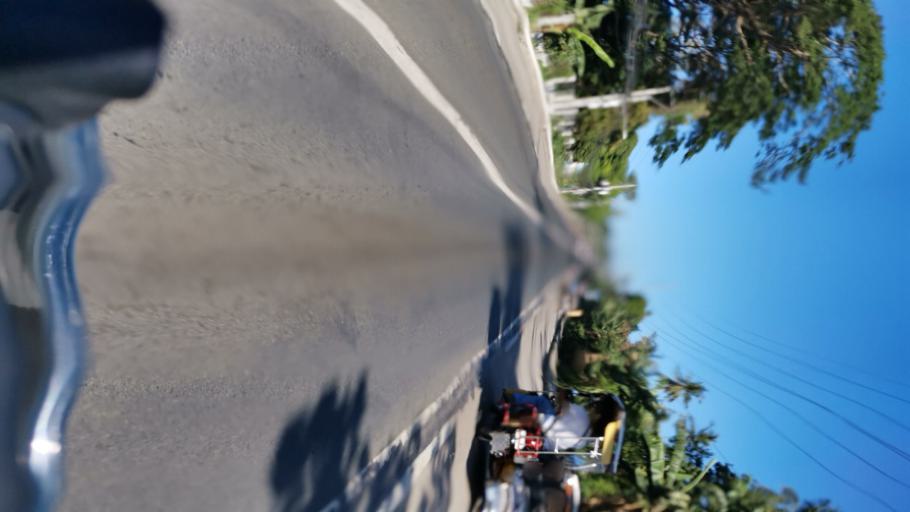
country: PH
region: Calabarzon
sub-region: Province of Batangas
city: Tanauan
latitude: 14.0872
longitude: 121.1290
